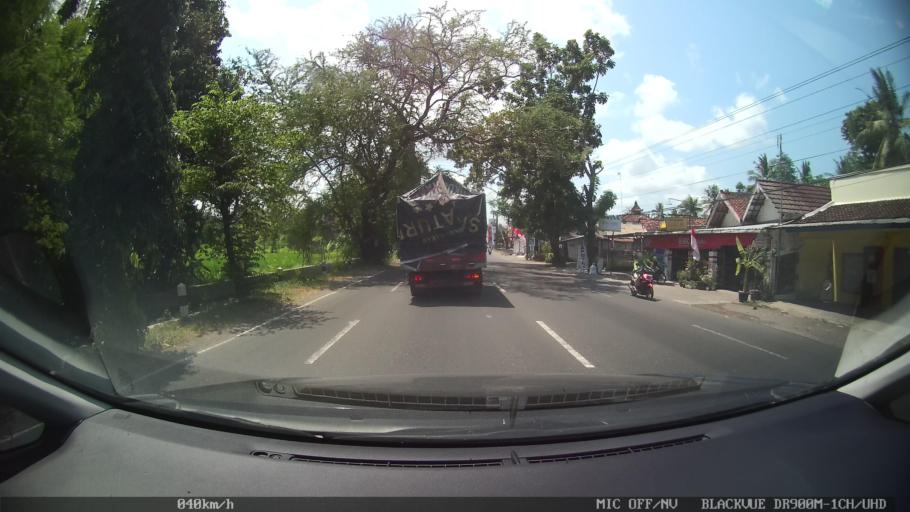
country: ID
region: Daerah Istimewa Yogyakarta
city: Pandak
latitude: -7.9112
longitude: 110.2925
